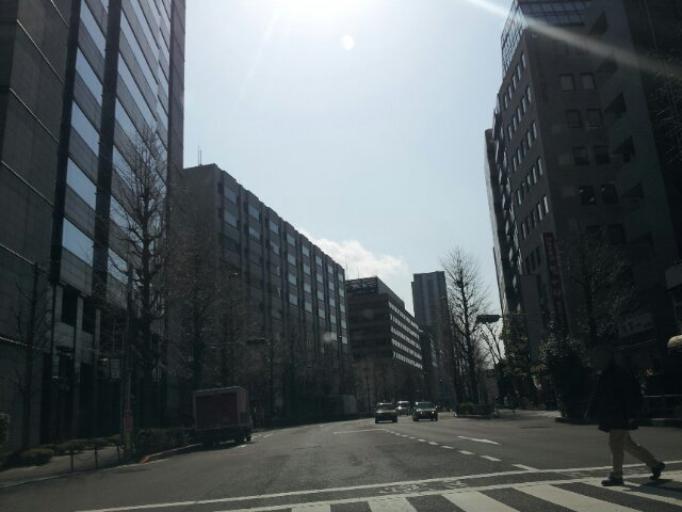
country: JP
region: Tokyo
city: Tokyo
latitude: 35.6649
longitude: 139.7466
